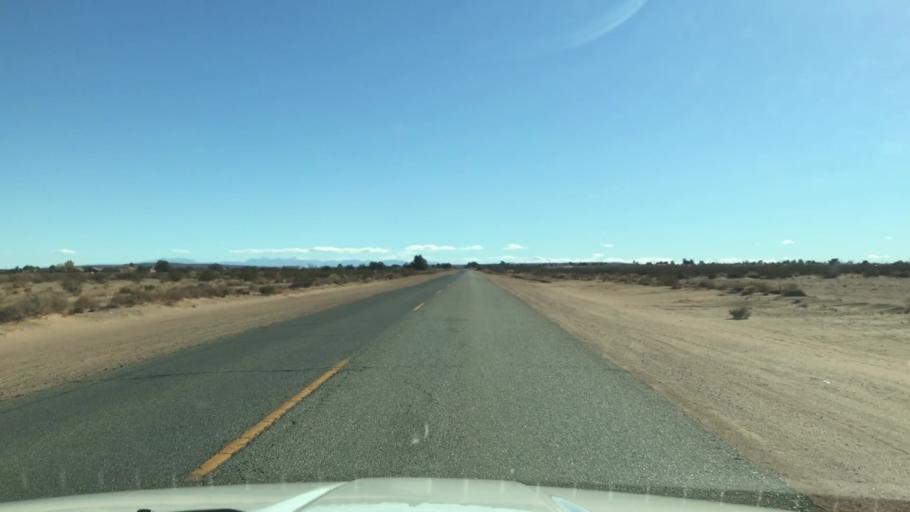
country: US
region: California
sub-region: Kern County
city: California City
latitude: 35.1466
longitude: -117.9859
